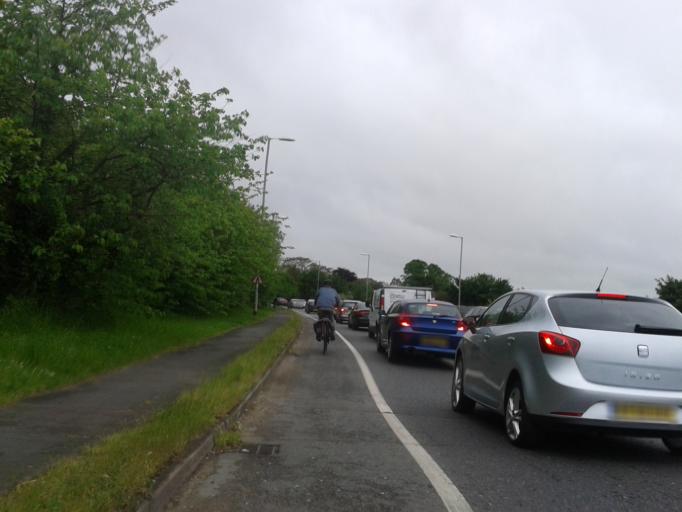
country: GB
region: England
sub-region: Cambridgeshire
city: Histon
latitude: 52.2322
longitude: 0.1119
